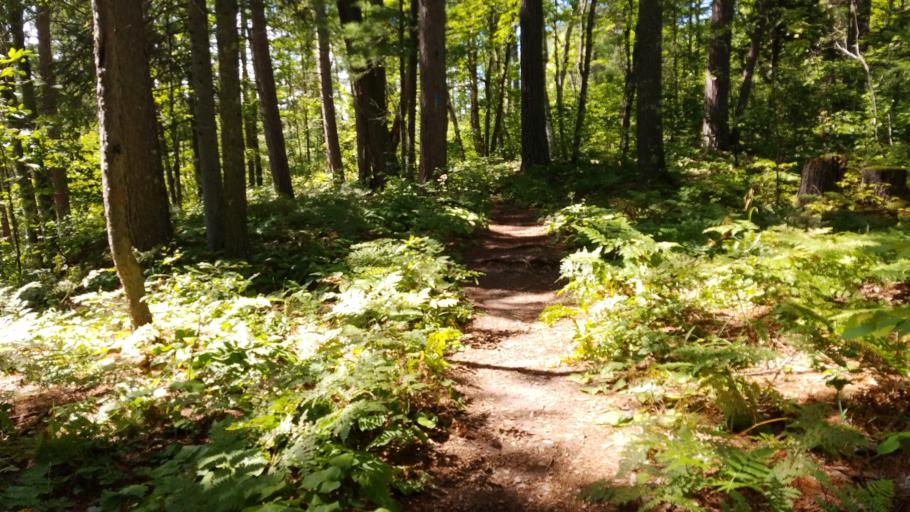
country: US
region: Michigan
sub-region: Ontonagon County
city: Ontonagon
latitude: 46.6506
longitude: -89.1544
